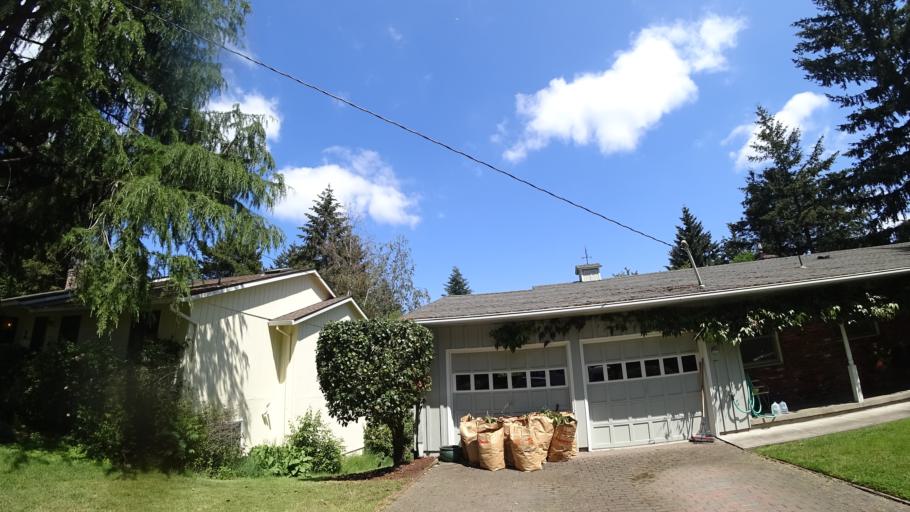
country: US
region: Oregon
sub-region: Washington County
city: Garden Home-Whitford
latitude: 45.4691
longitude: -122.7038
